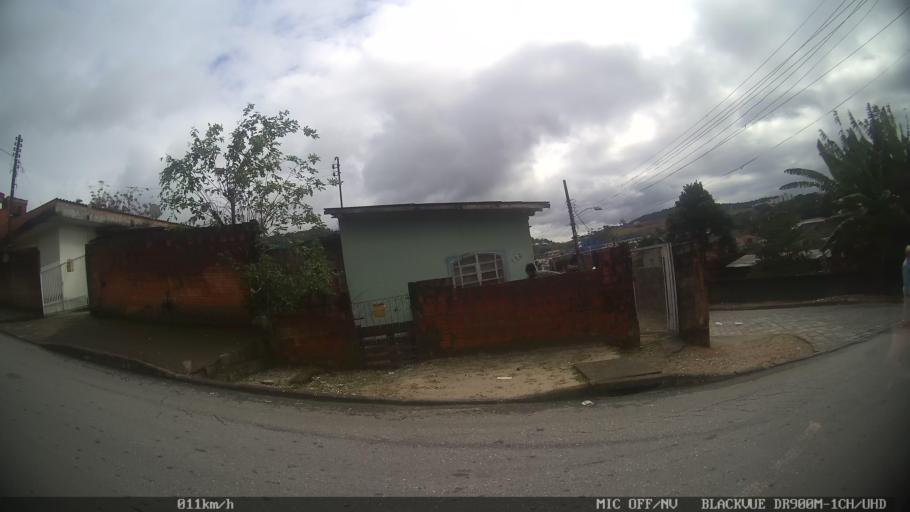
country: BR
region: Santa Catarina
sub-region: Biguacu
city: Biguacu
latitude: -27.5400
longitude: -48.6463
